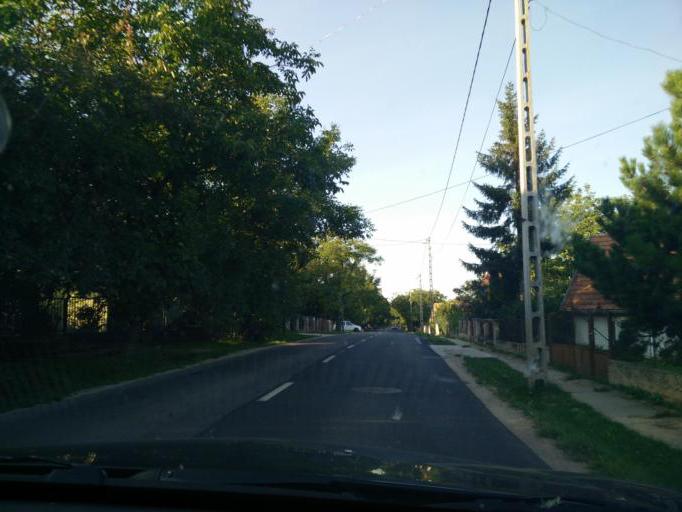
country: HU
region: Pest
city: Zsambek
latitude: 47.5614
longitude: 18.7299
